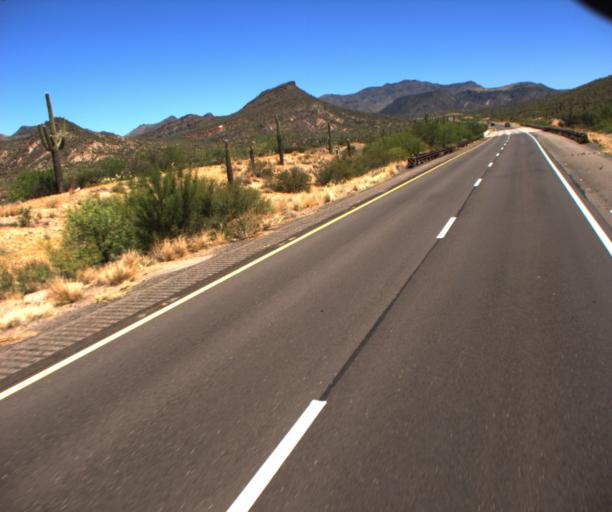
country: US
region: Arizona
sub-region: Maricopa County
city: Rio Verde
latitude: 33.7693
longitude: -111.4933
